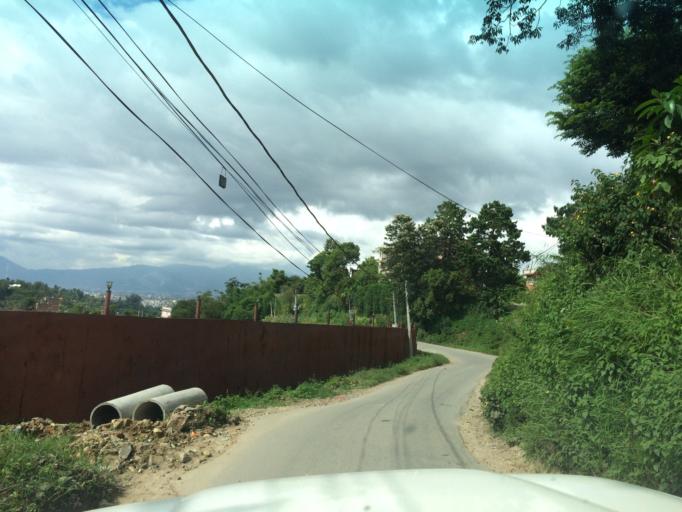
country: NP
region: Central Region
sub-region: Bagmati Zone
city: Patan
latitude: 27.6270
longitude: 85.3056
